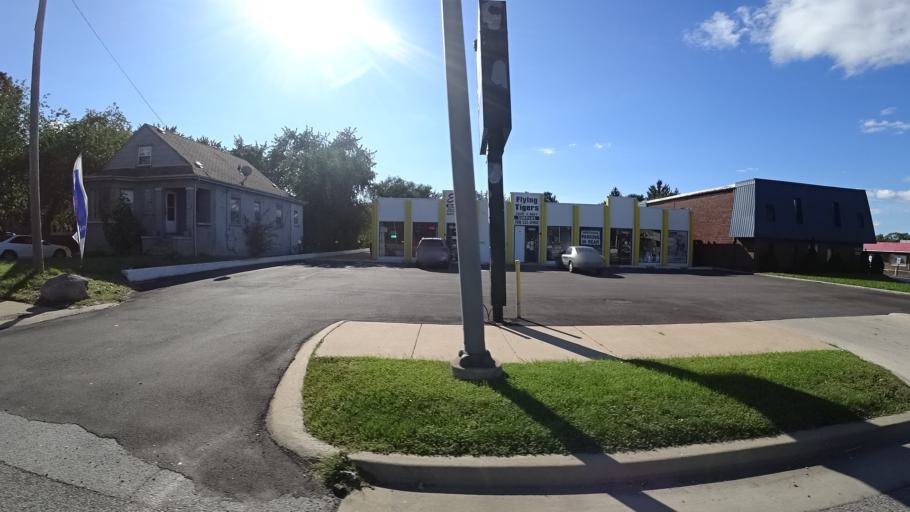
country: US
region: Illinois
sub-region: Cook County
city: Midlothian
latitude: 41.6226
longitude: -87.7373
